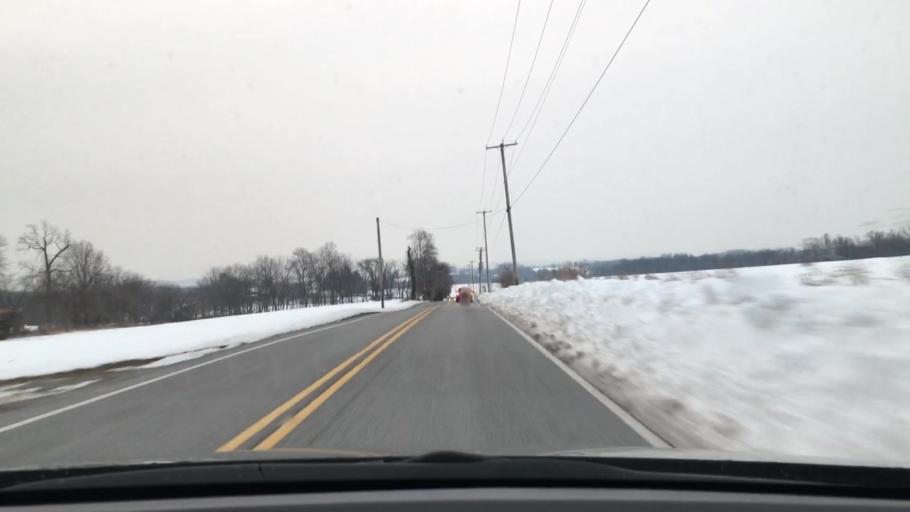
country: US
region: Pennsylvania
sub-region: York County
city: Weigelstown
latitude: 39.9710
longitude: -76.8482
